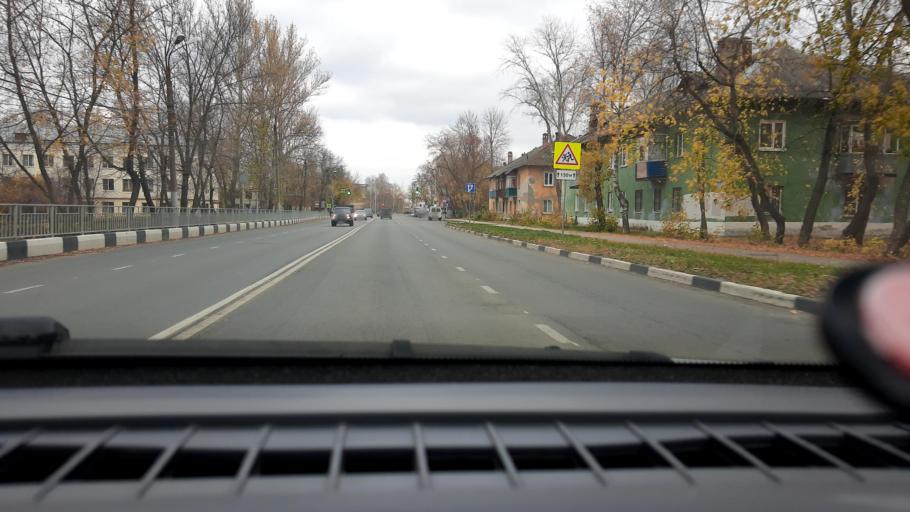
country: RU
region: Nizjnij Novgorod
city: Kstovo
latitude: 56.1551
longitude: 44.1945
